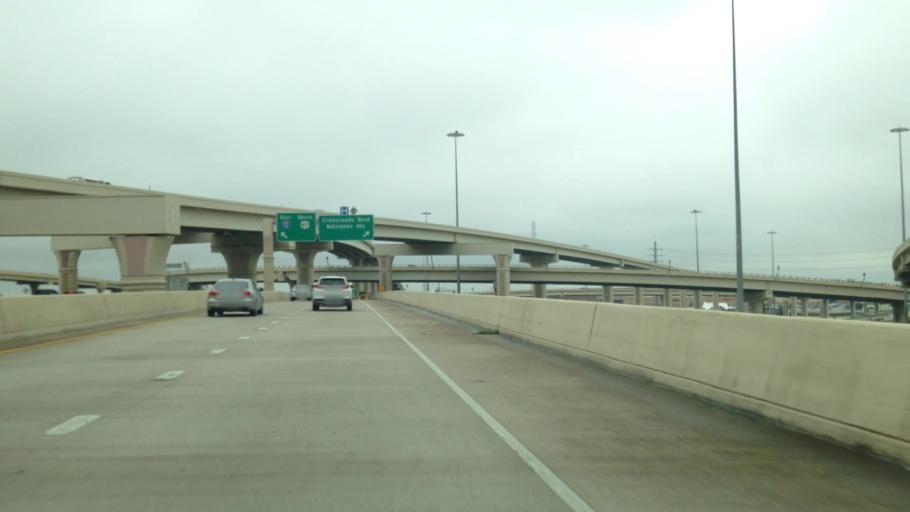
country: US
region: Texas
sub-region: Bexar County
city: Balcones Heights
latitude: 29.5020
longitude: -98.5496
